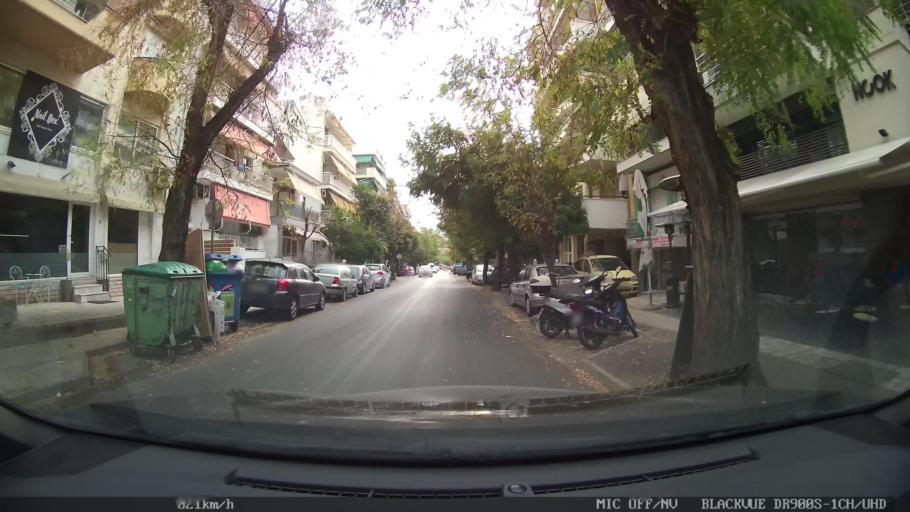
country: GR
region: Central Macedonia
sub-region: Nomos Thessalonikis
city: Triandria
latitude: 40.6092
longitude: 22.9750
